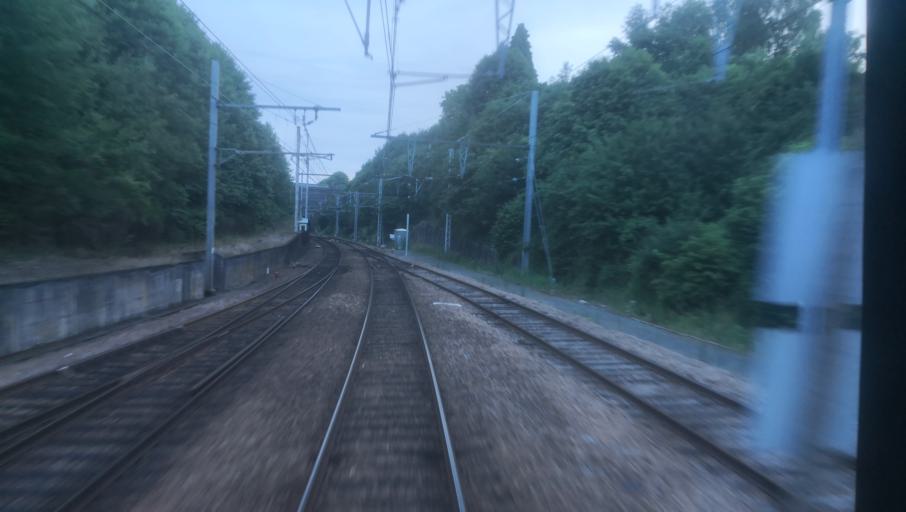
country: FR
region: Limousin
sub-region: Departement de la Haute-Vienne
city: Ambazac
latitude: 46.0515
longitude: 1.4704
